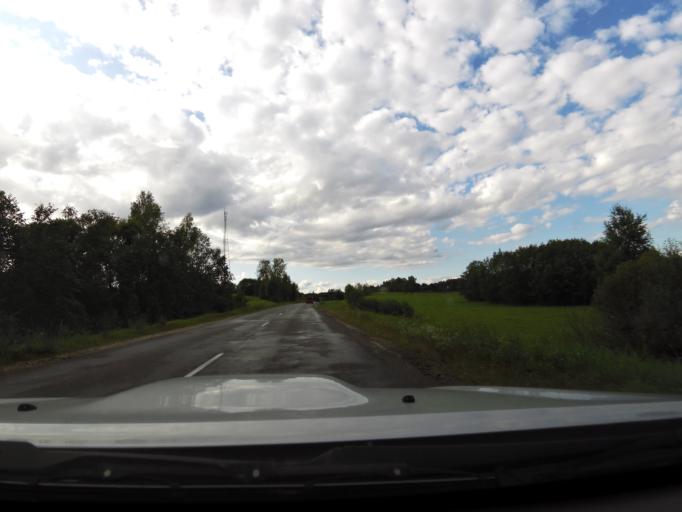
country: LV
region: Akniste
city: Akniste
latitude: 56.0128
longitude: 25.9294
